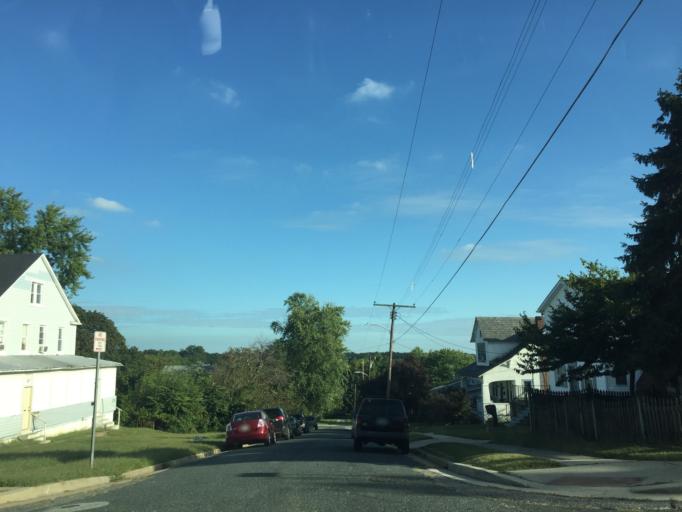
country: US
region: Maryland
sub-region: Baltimore County
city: Overlea
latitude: 39.3557
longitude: -76.5262
